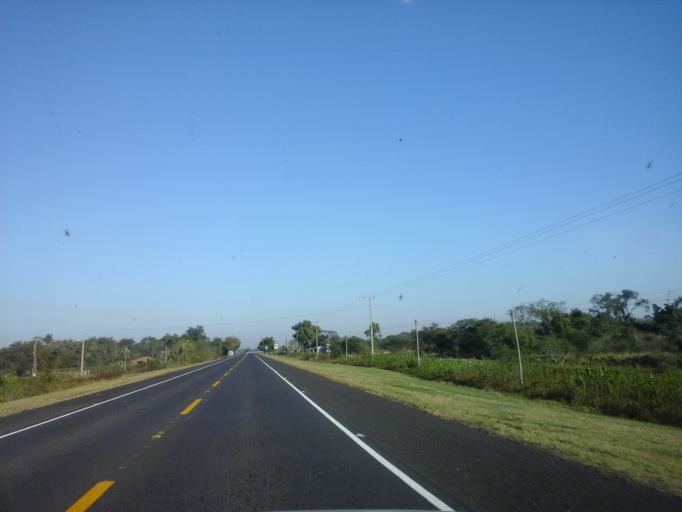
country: PY
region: Neembucu
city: Pilar
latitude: -26.8652
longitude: -58.1437
